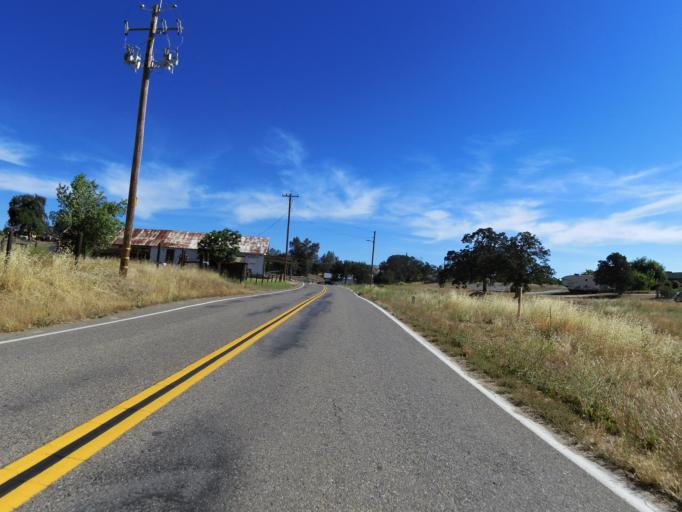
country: US
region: California
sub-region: Madera County
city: Yosemite Lakes
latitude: 37.2174
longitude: -119.9065
